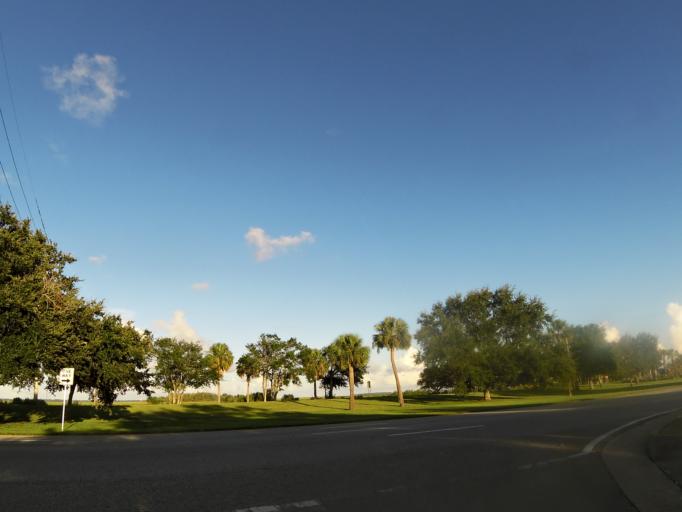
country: US
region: Georgia
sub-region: Glynn County
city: Brunswick
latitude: 31.1549
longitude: -81.4796
